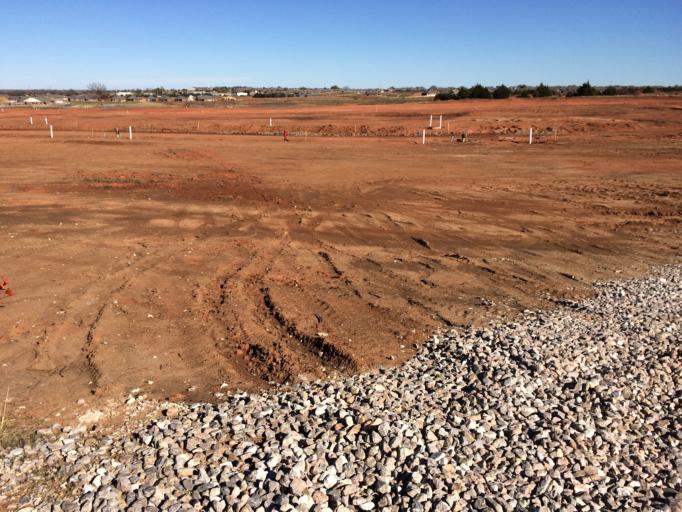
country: US
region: Oklahoma
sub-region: Cleveland County
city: Norman
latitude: 35.2552
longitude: -97.4589
